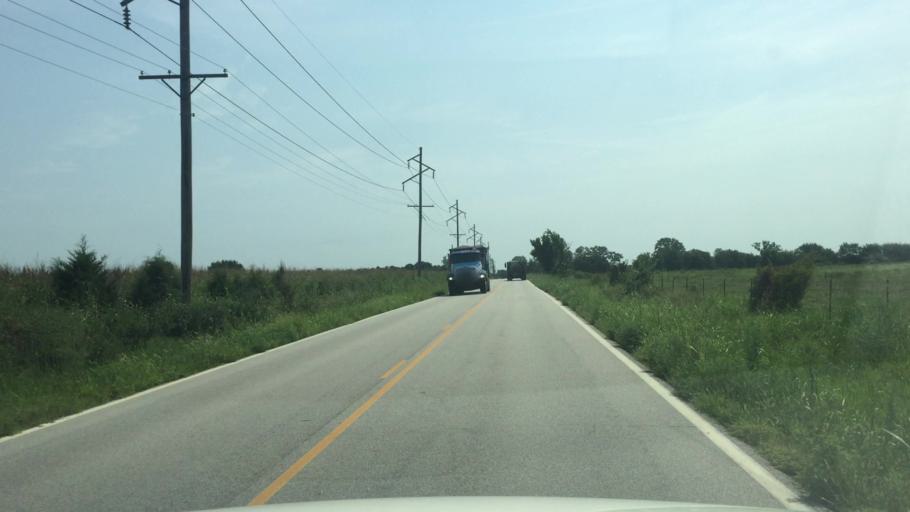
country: US
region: Kansas
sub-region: Montgomery County
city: Cherryvale
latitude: 37.2085
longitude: -95.5741
